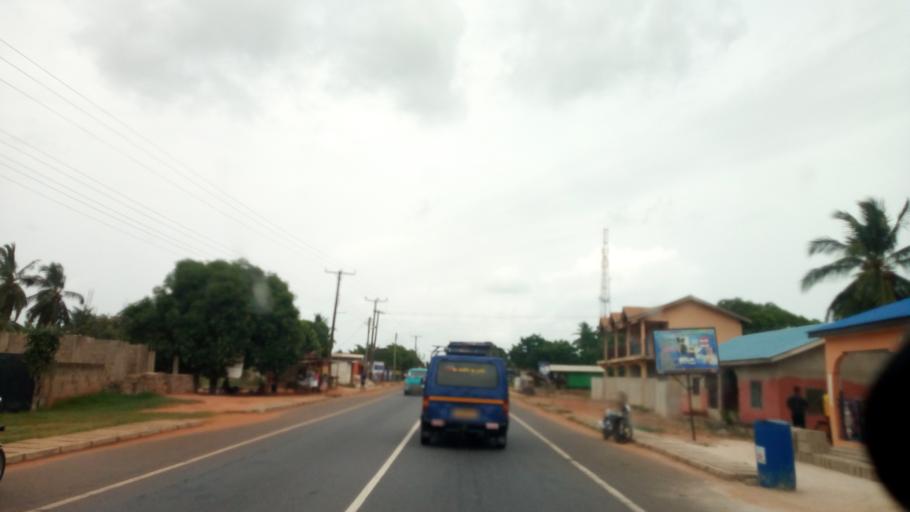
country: GH
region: Volta
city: Keta
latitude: 6.0642
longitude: 0.9133
